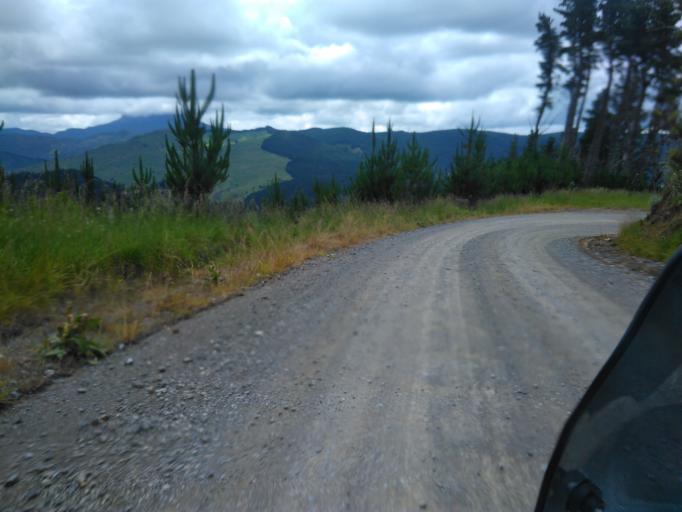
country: NZ
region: Gisborne
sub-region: Gisborne District
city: Gisborne
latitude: -38.0533
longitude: 178.1030
